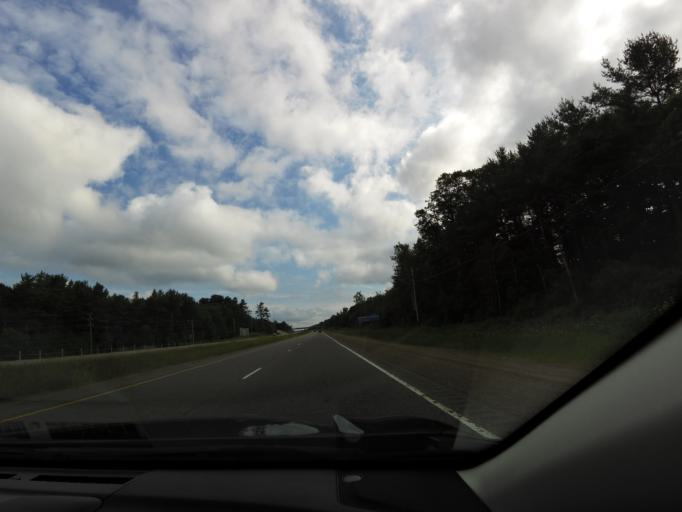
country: CA
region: Ontario
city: Bracebridge
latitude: 45.0051
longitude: -79.3005
